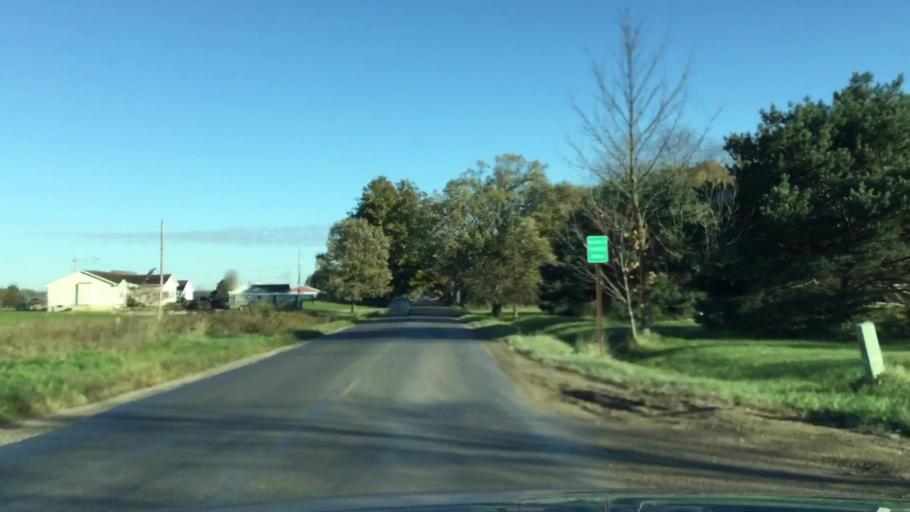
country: US
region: Michigan
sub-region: Genesee County
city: Argentine
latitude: 42.7805
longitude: -83.9423
